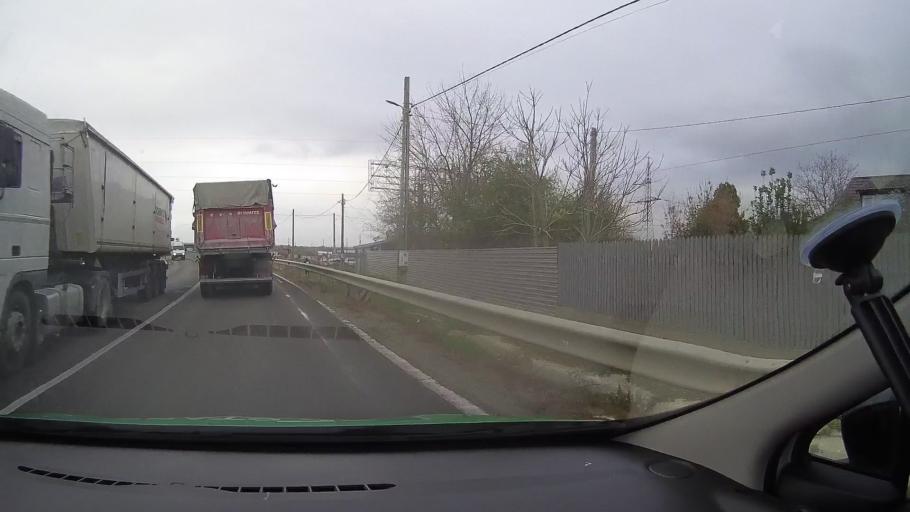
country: RO
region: Constanta
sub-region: Comuna Poarta Alba
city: Poarta Alba
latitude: 44.2121
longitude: 28.3946
